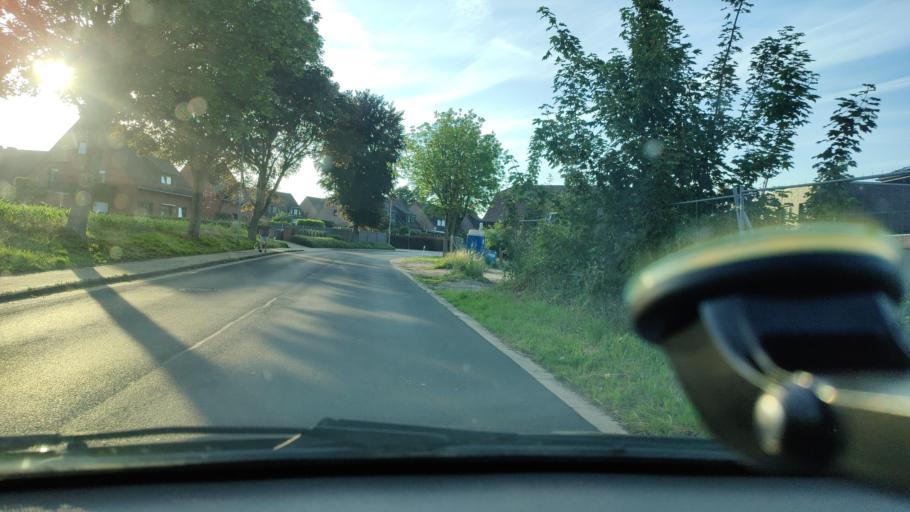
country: DE
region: North Rhine-Westphalia
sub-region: Regierungsbezirk Dusseldorf
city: Rheurdt
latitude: 51.4612
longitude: 6.4751
